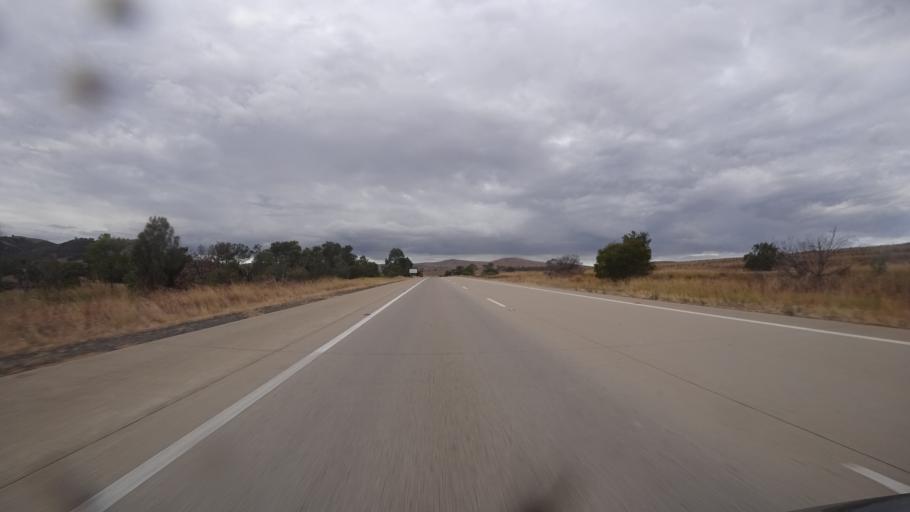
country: AU
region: New South Wales
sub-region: Yass Valley
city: Yass
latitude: -34.8198
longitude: 148.6658
